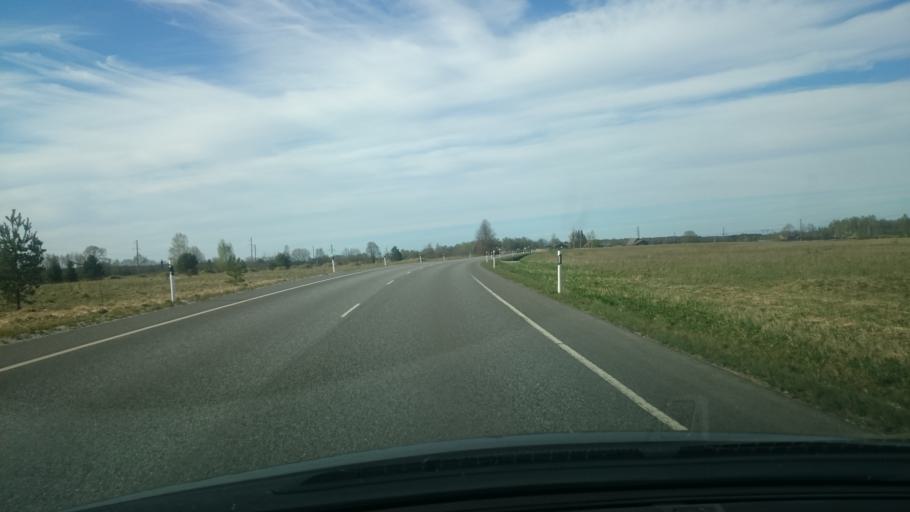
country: EE
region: Ida-Virumaa
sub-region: Johvi vald
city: Johvi
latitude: 59.2601
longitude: 27.5147
